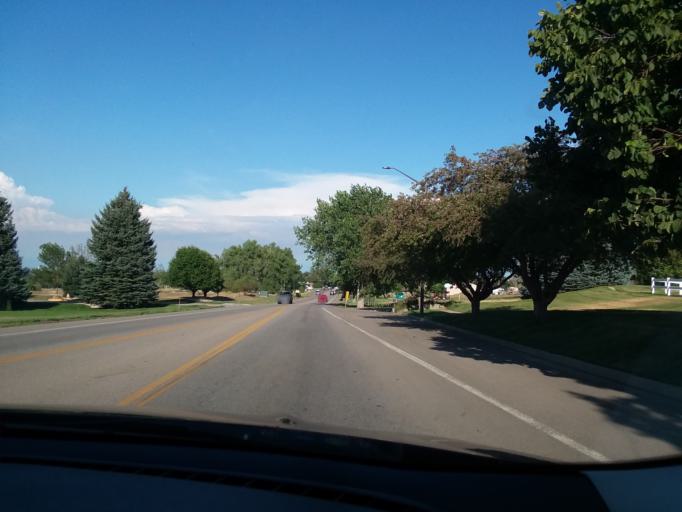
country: US
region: Colorado
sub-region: Larimer County
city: Fort Collins
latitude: 40.4947
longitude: -105.0827
